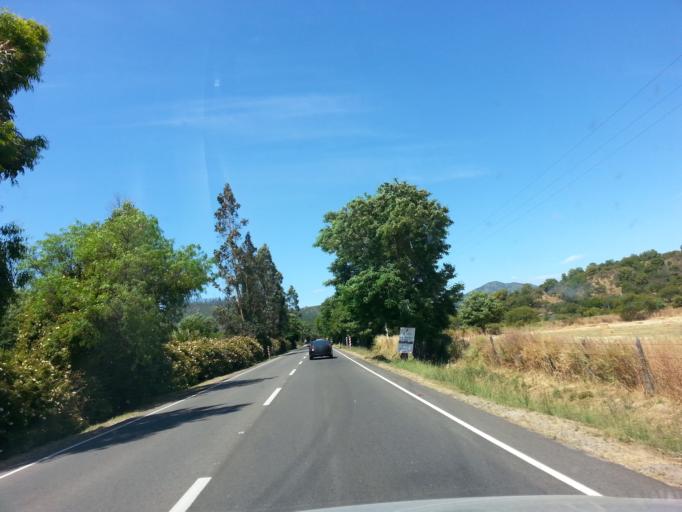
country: CL
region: Valparaiso
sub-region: Provincia de Marga Marga
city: Quilpue
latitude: -33.2341
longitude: -71.4351
